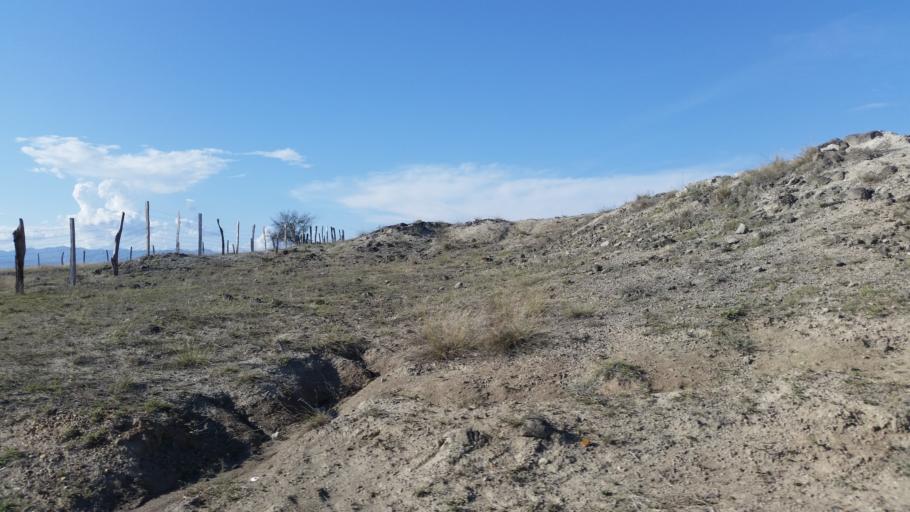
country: CO
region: Huila
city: Villavieja
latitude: 3.2331
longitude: -75.1204
